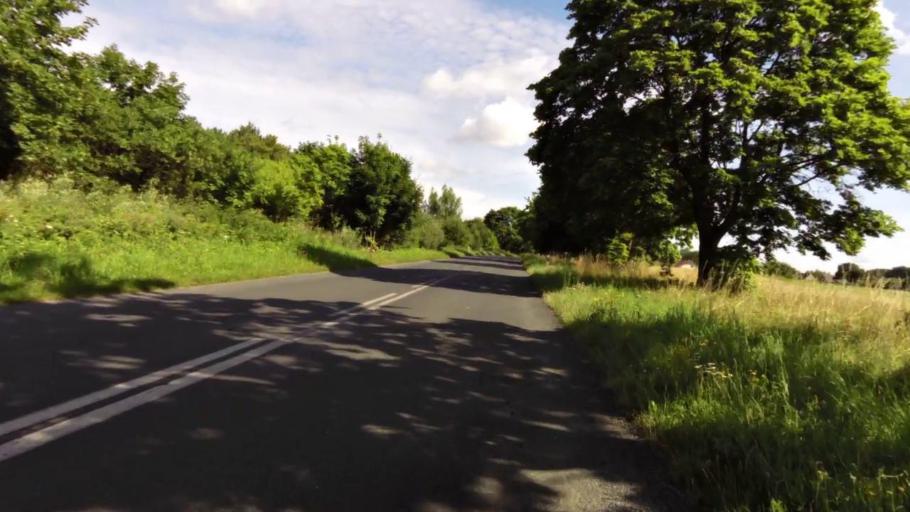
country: PL
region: West Pomeranian Voivodeship
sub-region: Powiat stargardzki
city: Dobrzany
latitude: 53.3771
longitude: 15.4354
